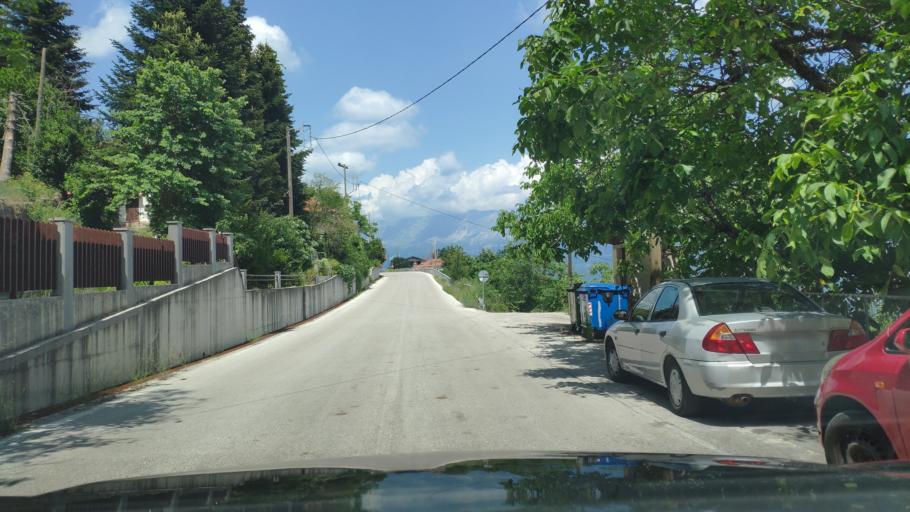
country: GR
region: Epirus
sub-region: Nomos Artas
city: Agios Dimitrios
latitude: 39.3258
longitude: 20.9961
